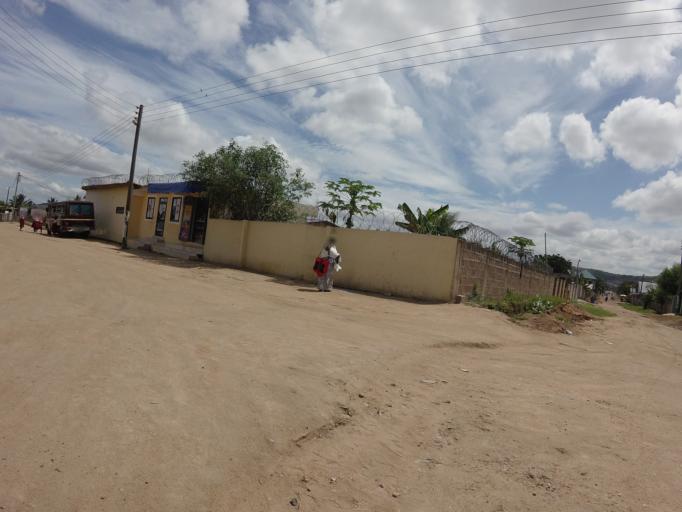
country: GH
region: Central
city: Kasoa
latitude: 5.5446
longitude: -0.4013
